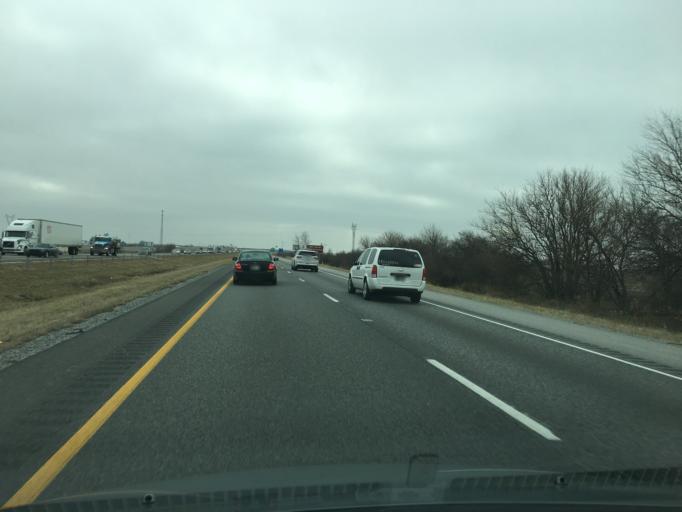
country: US
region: Indiana
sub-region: Jasper County
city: Remington
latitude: 40.7772
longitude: -87.1270
